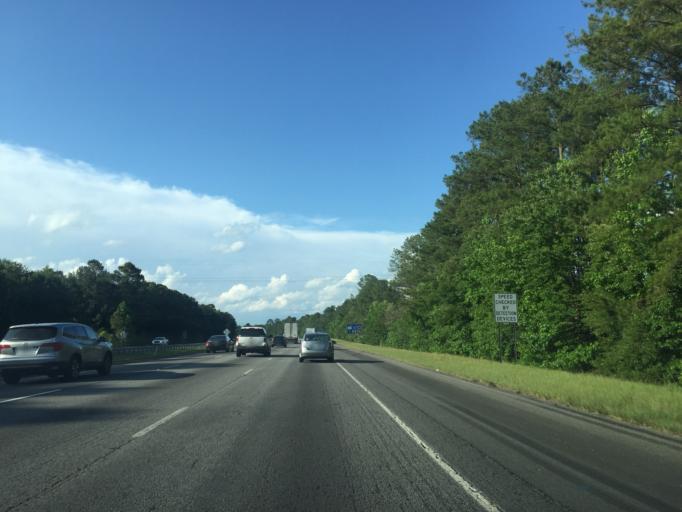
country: US
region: Georgia
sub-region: Chatham County
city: Pooler
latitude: 32.0876
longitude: -81.2391
